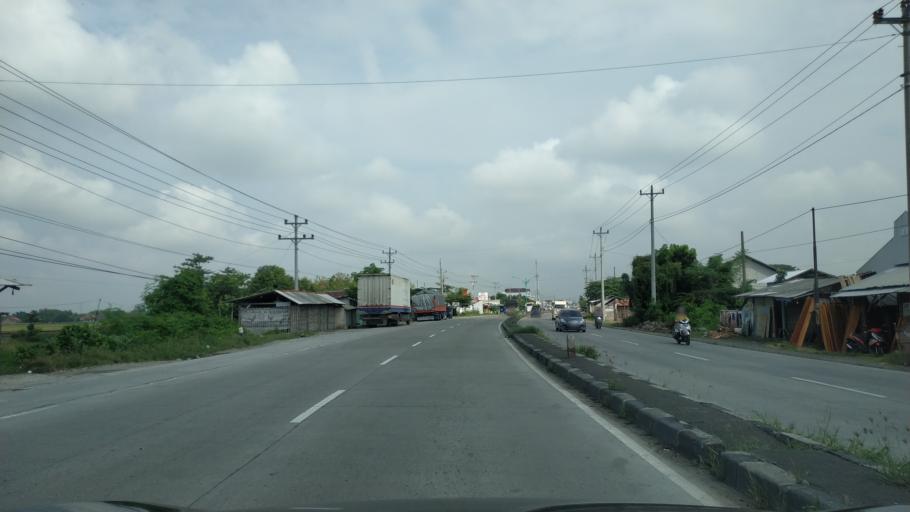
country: ID
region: Central Java
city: Bulakamba
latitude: -6.8755
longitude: 108.9534
